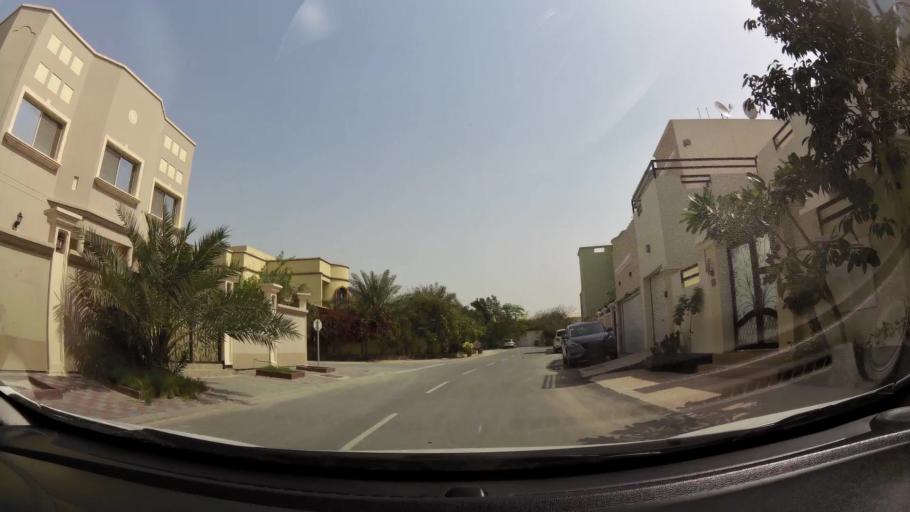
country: BH
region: Manama
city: Jidd Hafs
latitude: 26.2298
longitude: 50.5028
